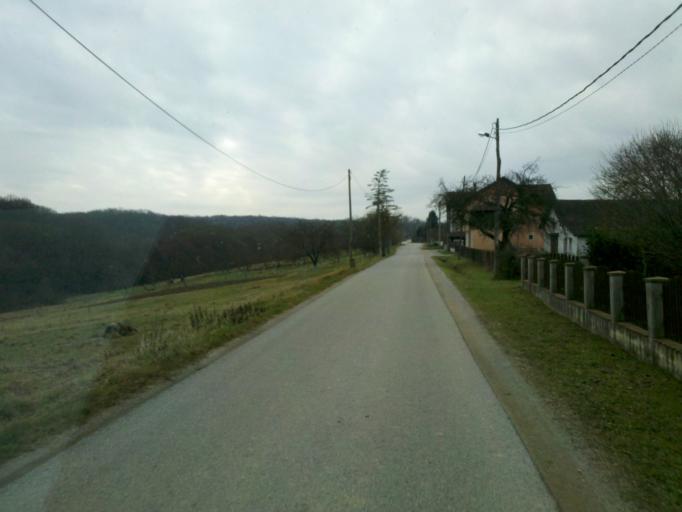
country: HR
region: Grad Zagreb
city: Horvati
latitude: 45.6652
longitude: 15.8217
